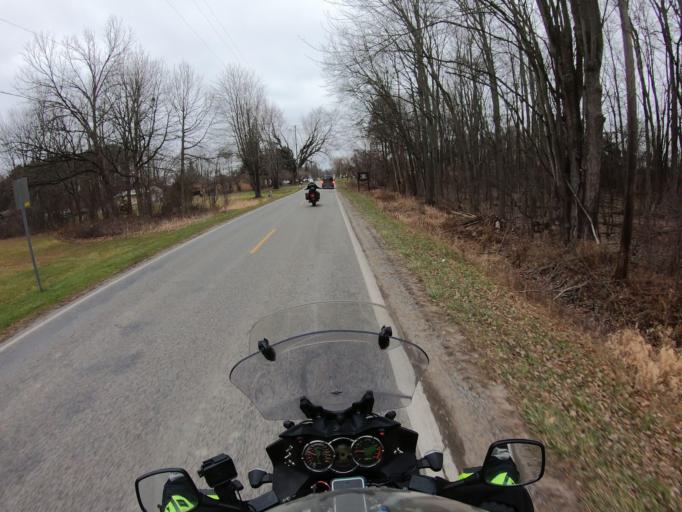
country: US
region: Michigan
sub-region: Saginaw County
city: Saint Charles
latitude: 43.2875
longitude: -84.1361
